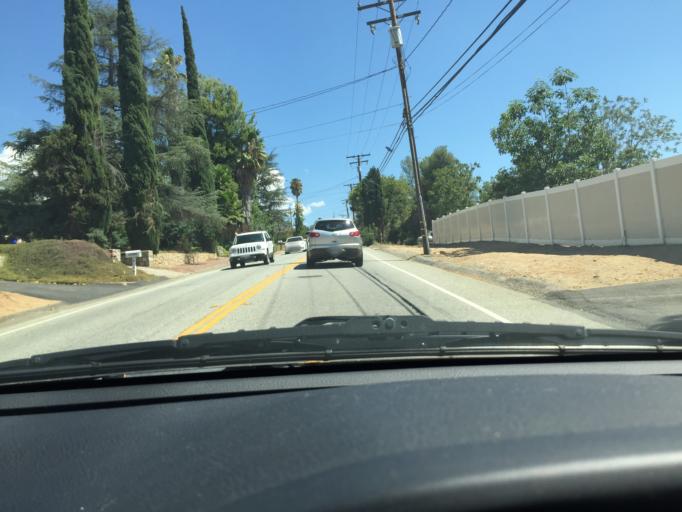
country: US
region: California
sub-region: San Bernardino County
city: Yucaipa
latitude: 34.0157
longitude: -117.0329
